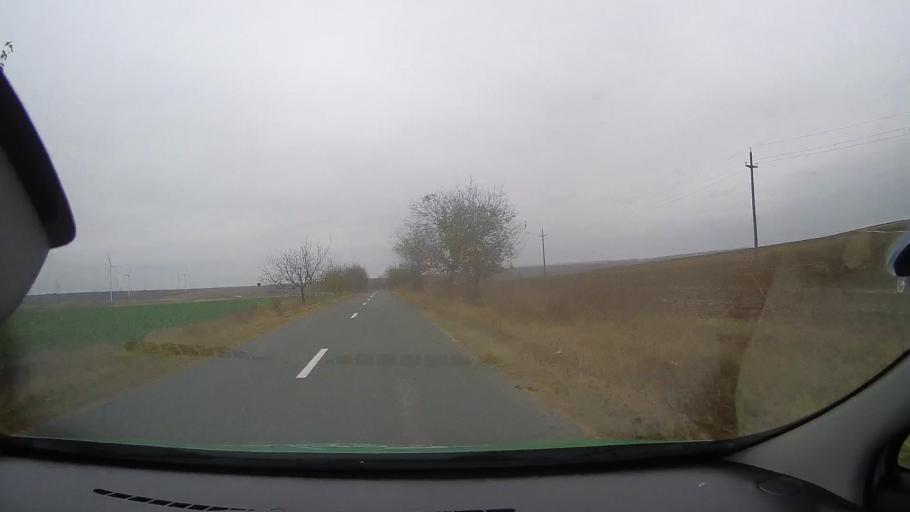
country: RO
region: Constanta
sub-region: Comuna Targusor
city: Targusor
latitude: 44.4813
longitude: 28.3722
